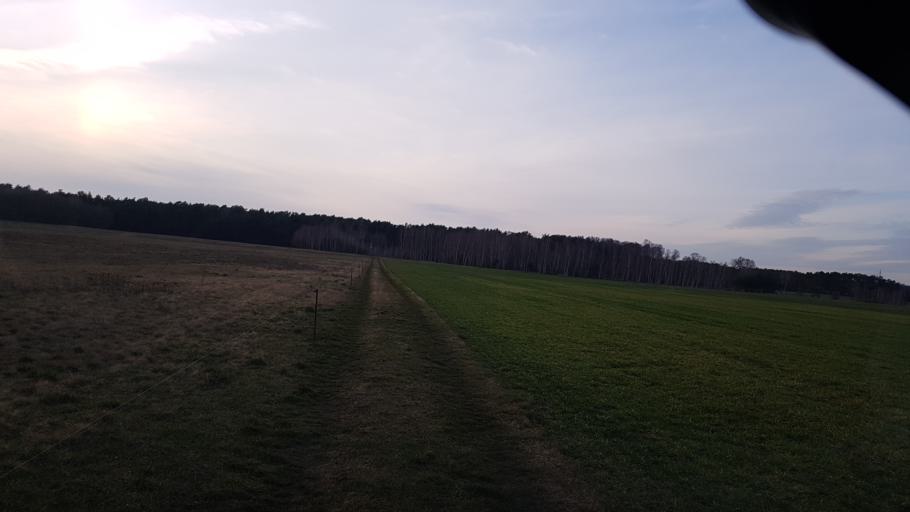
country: DE
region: Brandenburg
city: Schonborn
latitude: 51.5837
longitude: 13.4968
